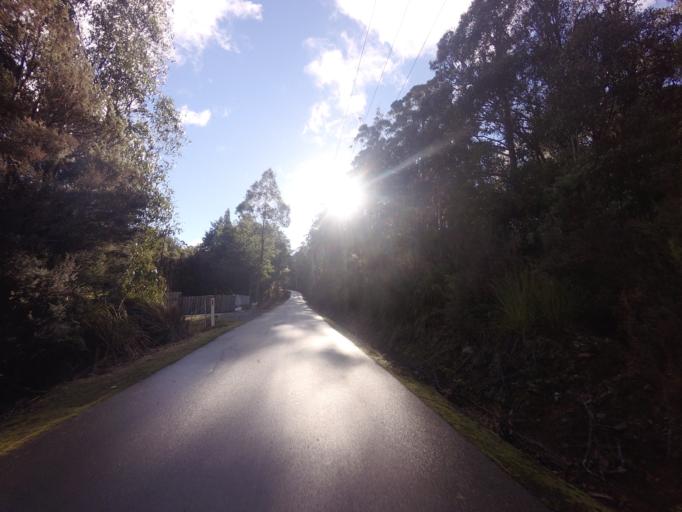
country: AU
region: Tasmania
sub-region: Glenorchy
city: Berriedale
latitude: -42.8487
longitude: 147.1677
